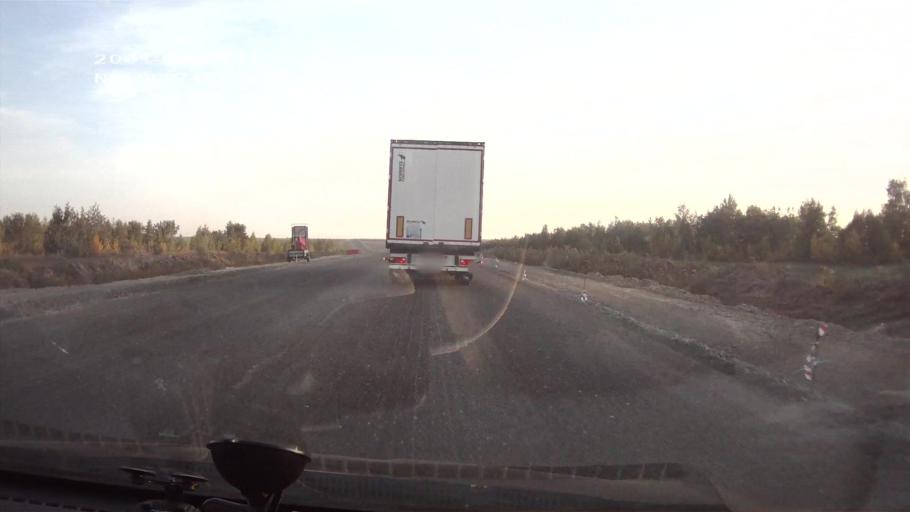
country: RU
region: Saratov
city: Krasnoarmeysk
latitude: 51.0001
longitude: 45.6139
